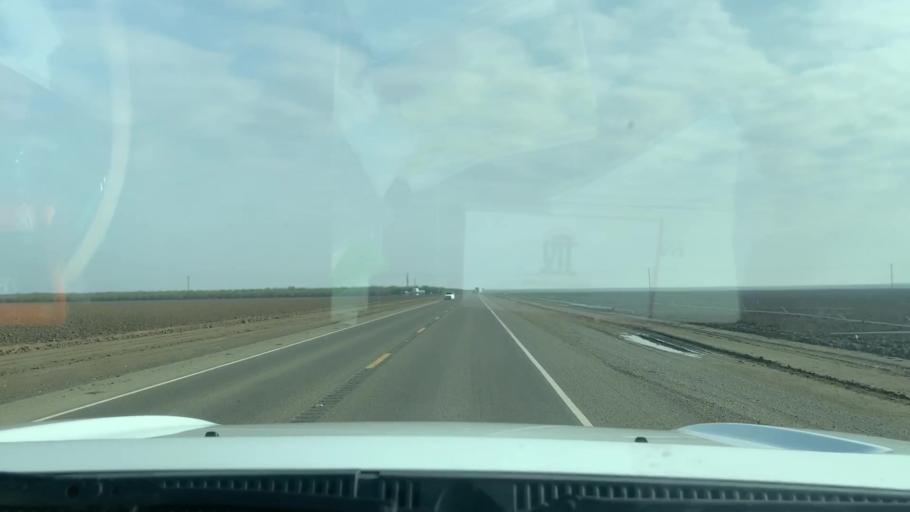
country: US
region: California
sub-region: Fresno County
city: Huron
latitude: 36.2554
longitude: -120.0719
